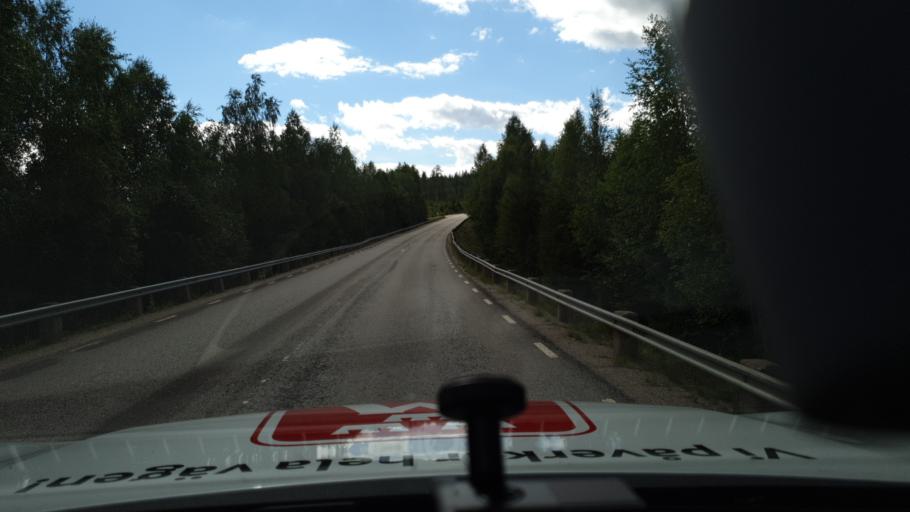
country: NO
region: Hedmark
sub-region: Trysil
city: Innbygda
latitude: 61.0191
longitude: 12.5365
